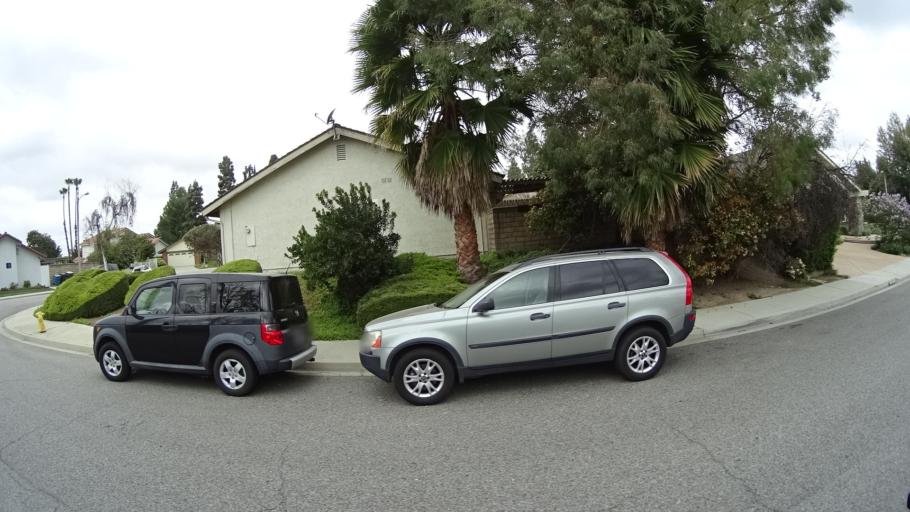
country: US
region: California
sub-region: Ventura County
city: Thousand Oaks
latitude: 34.2175
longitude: -118.8790
